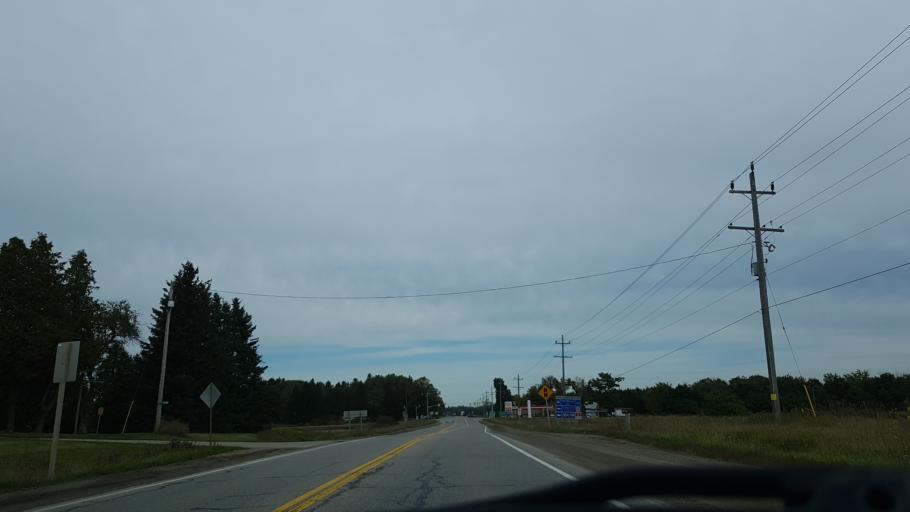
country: CA
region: Ontario
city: Orangeville
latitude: 43.8295
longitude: -80.0322
